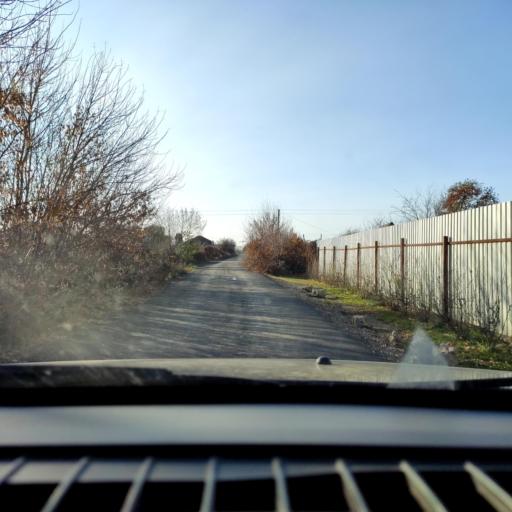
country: RU
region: Samara
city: Tol'yatti
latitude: 53.6642
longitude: 49.3417
